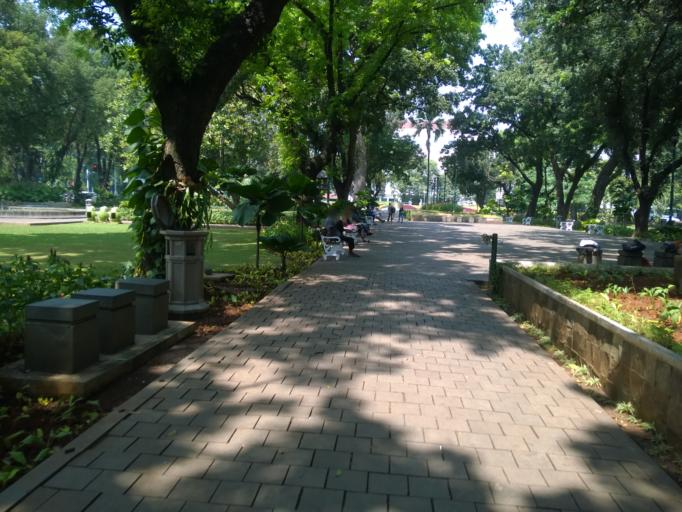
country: ID
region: Jakarta Raya
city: Jakarta
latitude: -6.1991
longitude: 106.8327
